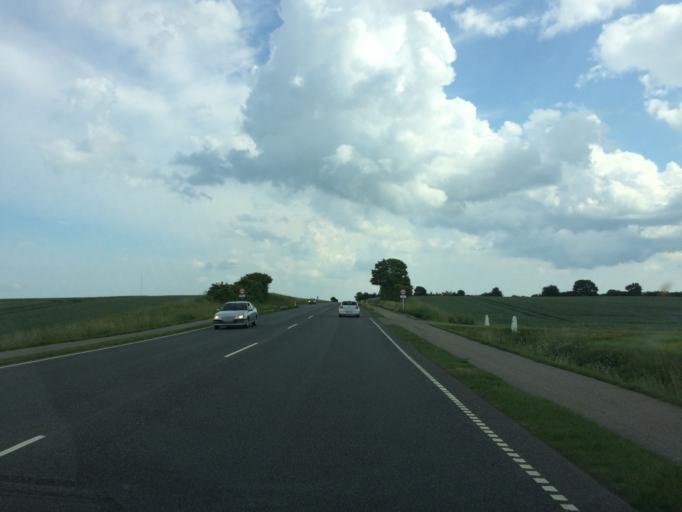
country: DK
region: South Denmark
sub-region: Vejle Kommune
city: Borkop
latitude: 55.6077
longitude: 9.6208
